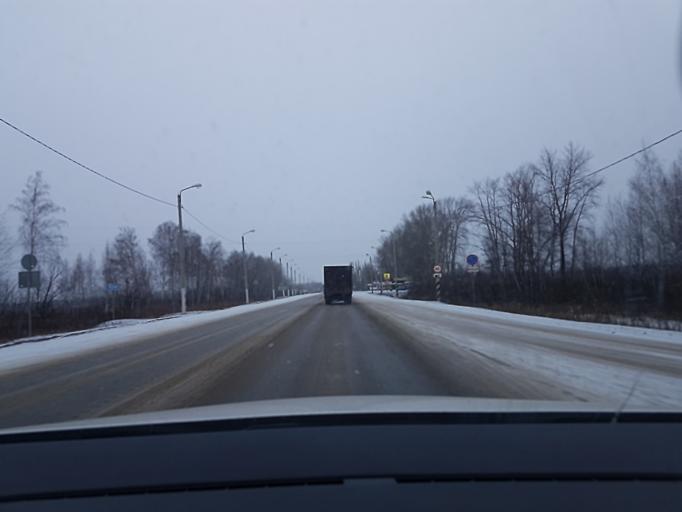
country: RU
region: Tambov
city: Pervomayskiy
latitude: 53.2459
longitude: 40.2534
